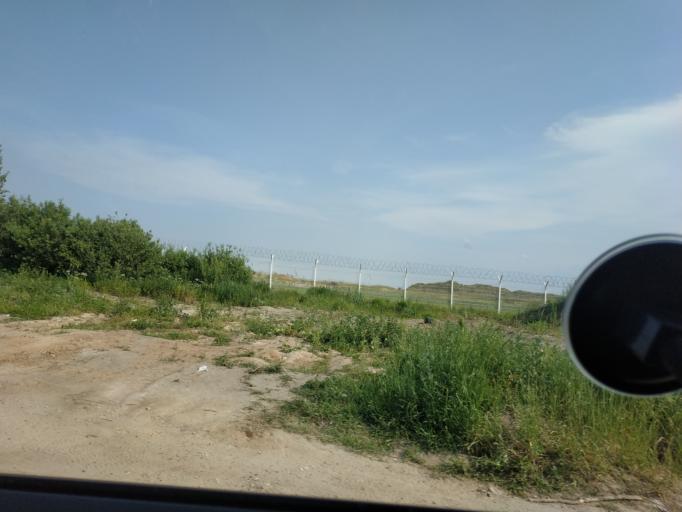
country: RU
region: Moskovskaya
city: Yakovlevskoye
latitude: 55.4310
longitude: 37.9040
